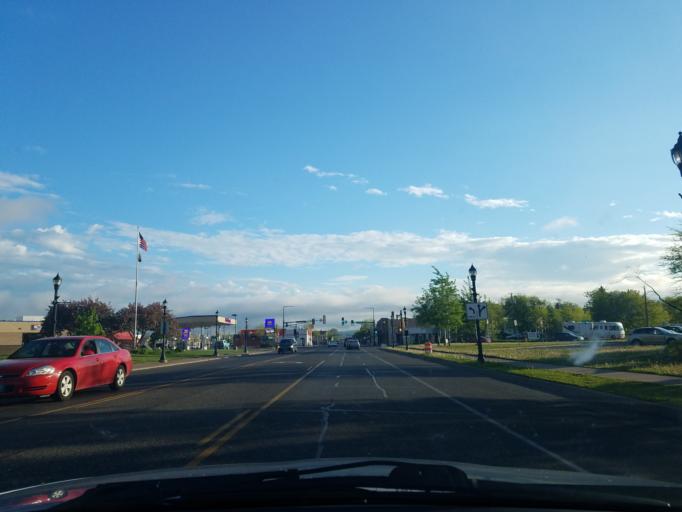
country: US
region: Minnesota
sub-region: Saint Louis County
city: Proctor
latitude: 46.7417
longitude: -92.1653
